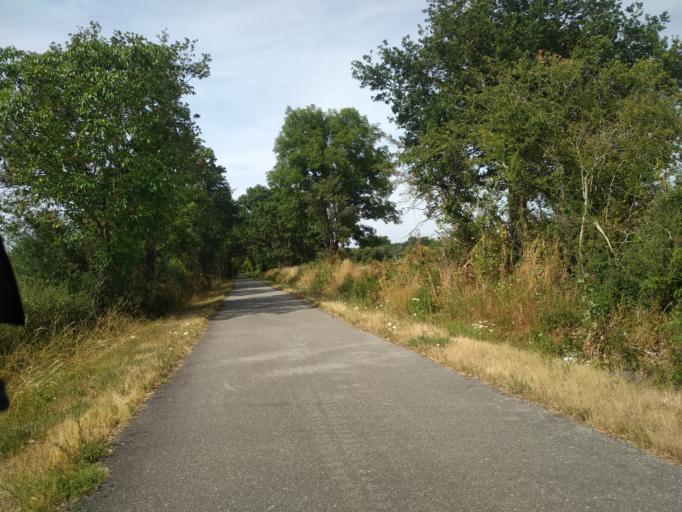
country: FR
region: Bourgogne
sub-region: Departement de Saone-et-Loire
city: Bourbon-Lancy
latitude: 46.5888
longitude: 3.7455
